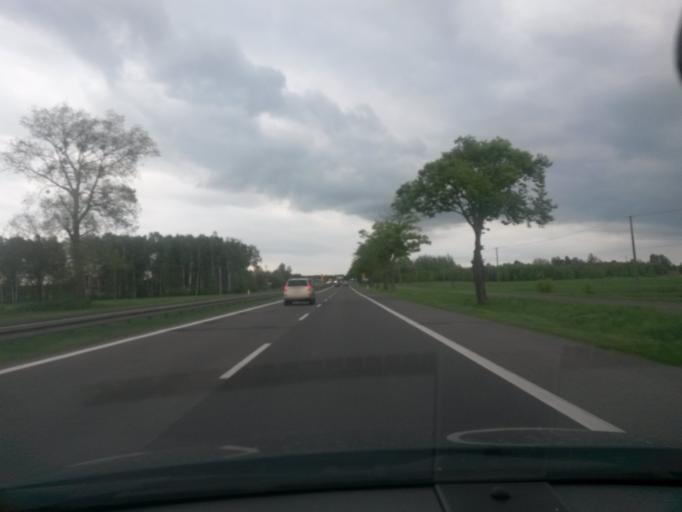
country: PL
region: Masovian Voivodeship
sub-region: Powiat plonski
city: Zaluski
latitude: 52.5825
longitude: 20.4669
